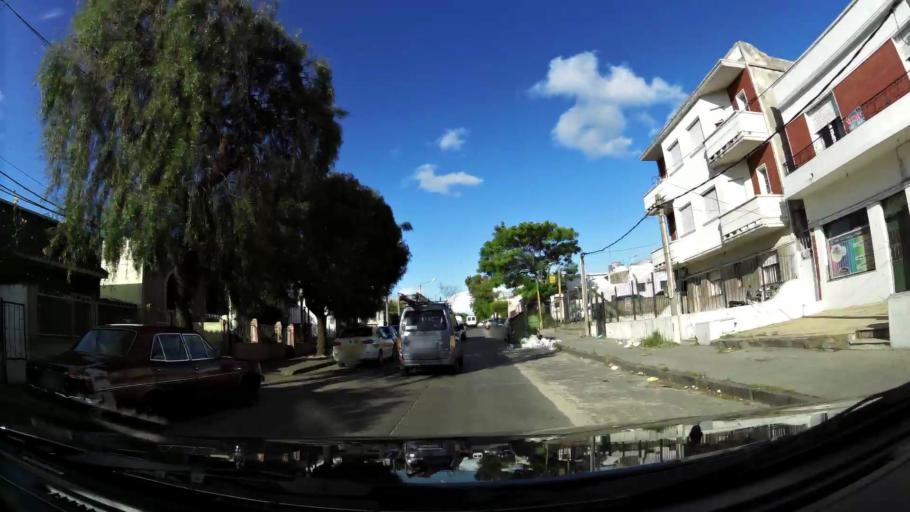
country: UY
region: Montevideo
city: Montevideo
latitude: -34.8753
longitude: -56.1449
